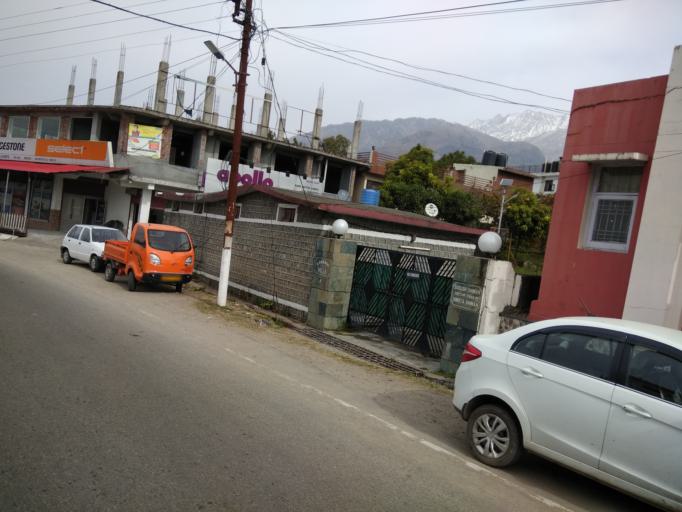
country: IN
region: Himachal Pradesh
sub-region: Kangra
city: Dharmsala
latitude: 32.1928
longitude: 76.3486
